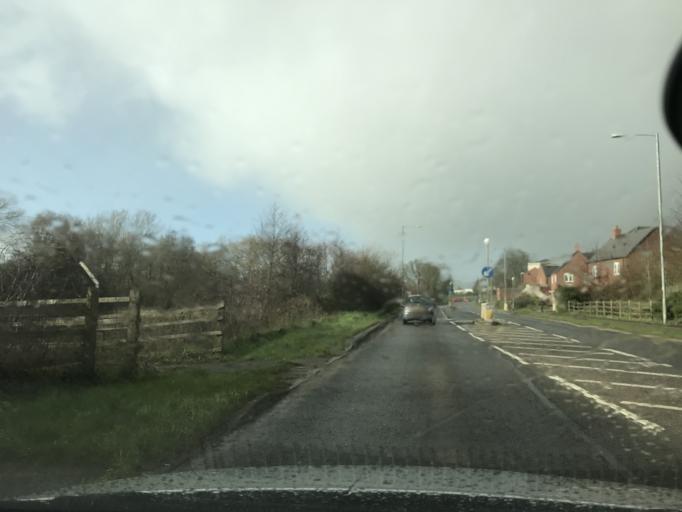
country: GB
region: England
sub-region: Somerset
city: Taunton
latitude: 51.0290
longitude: -3.1331
